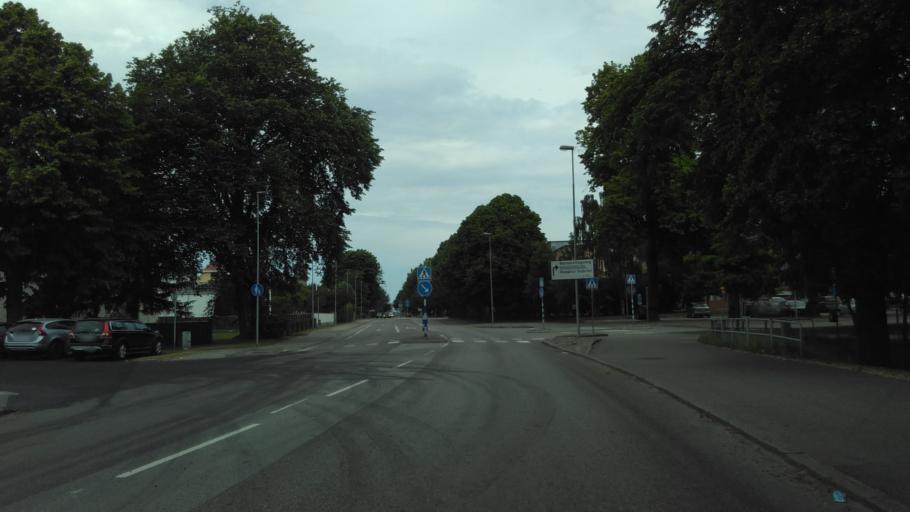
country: SE
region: Vaestra Goetaland
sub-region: Lidkopings Kommun
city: Lidkoping
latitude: 58.4962
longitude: 13.1492
